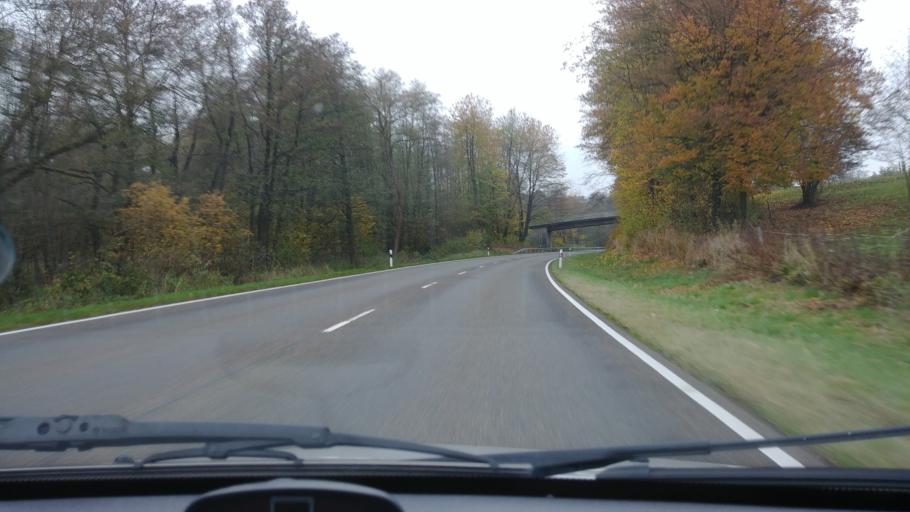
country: DE
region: Rheinland-Pfalz
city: Enspel
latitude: 50.6165
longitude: 7.8803
